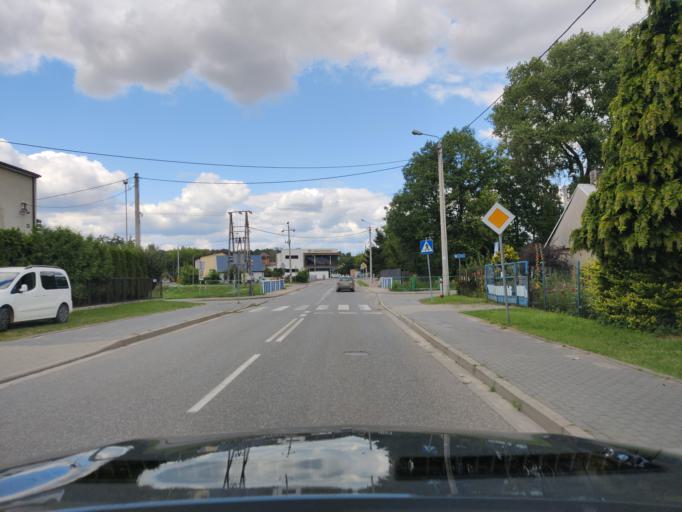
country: PL
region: Masovian Voivodeship
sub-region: Powiat wegrowski
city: Wegrow
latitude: 52.4022
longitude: 22.0203
